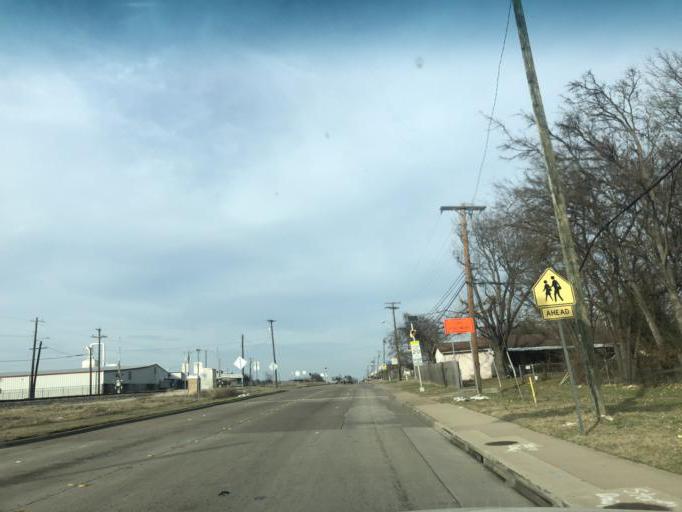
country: US
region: Texas
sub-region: Dallas County
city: Duncanville
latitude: 32.6655
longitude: -96.9058
